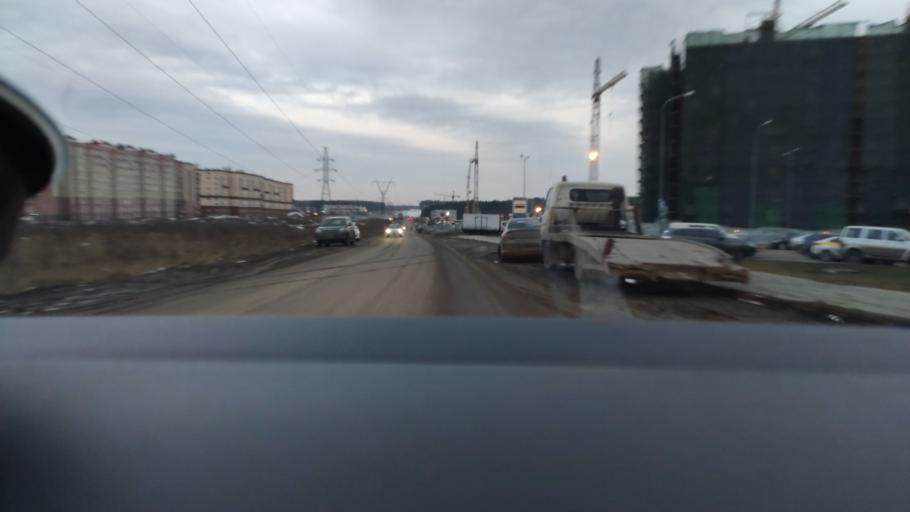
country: RU
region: Moscow
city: Zagor'ye
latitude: 55.5354
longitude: 37.6371
